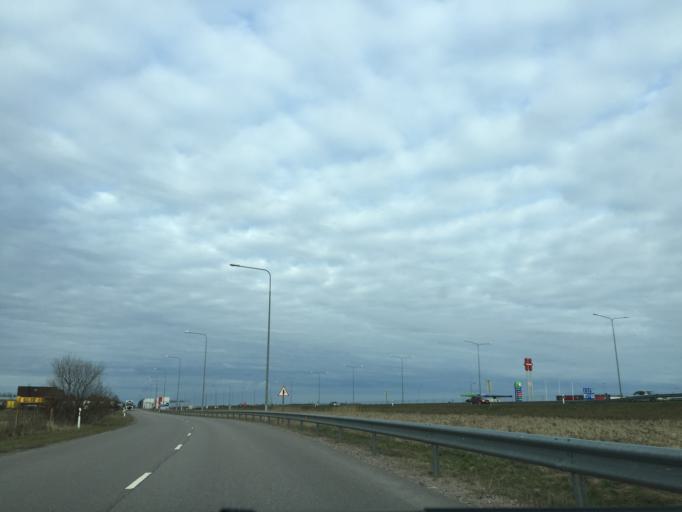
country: LT
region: Klaipedos apskritis
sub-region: Klaipeda
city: Klaipeda
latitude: 55.7070
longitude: 21.2351
